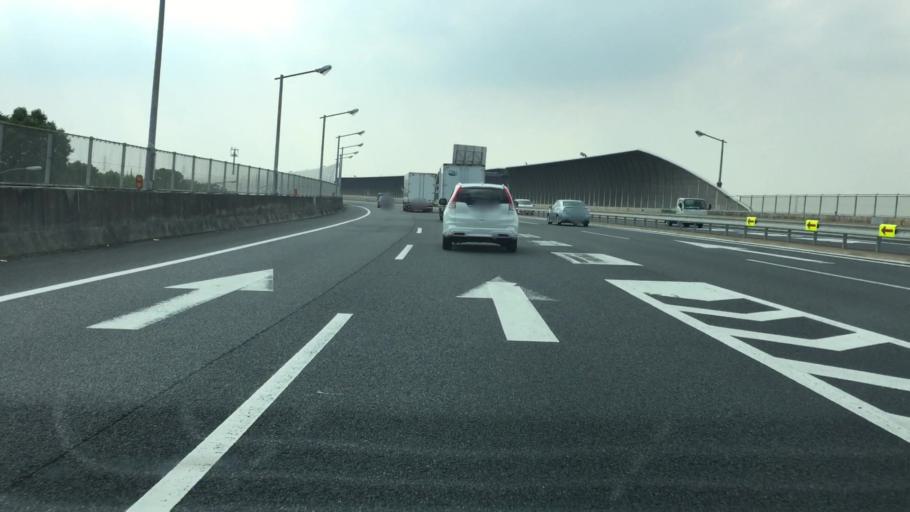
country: JP
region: Saitama
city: Yashio-shi
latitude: 35.8424
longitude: 139.8525
